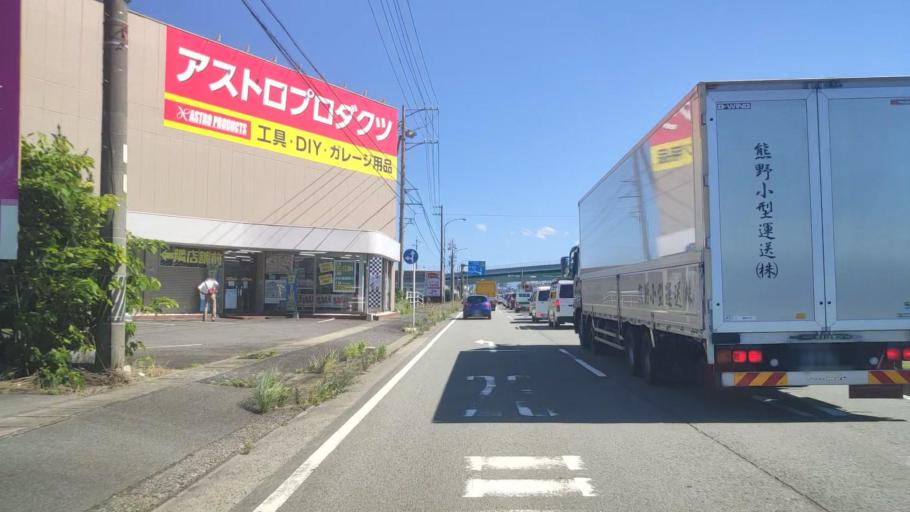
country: JP
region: Mie
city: Hisai-motomachi
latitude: 34.6173
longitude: 136.5159
